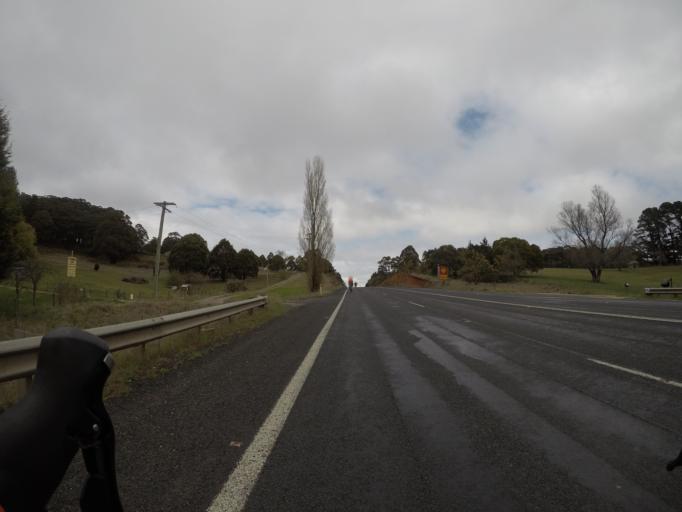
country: AU
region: New South Wales
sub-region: Lithgow
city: Portland
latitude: -33.4411
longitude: 149.8376
